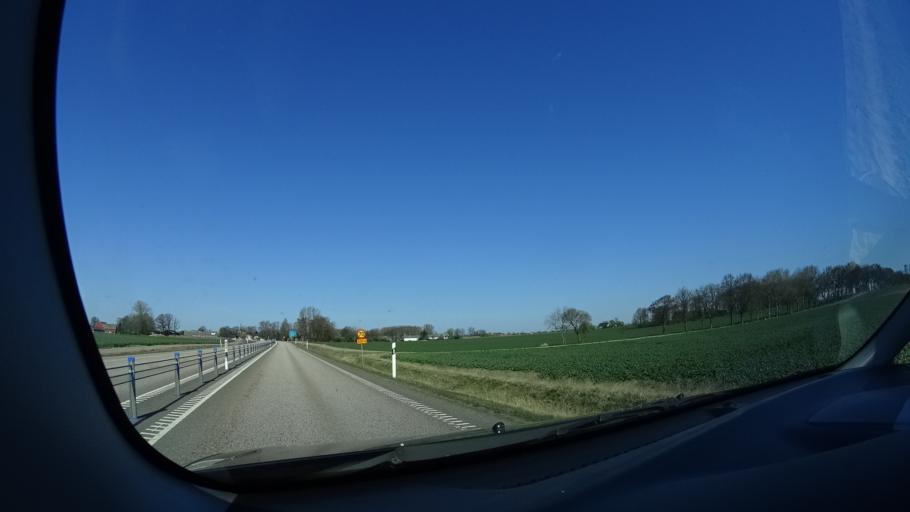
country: SE
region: Skane
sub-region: Angelholms Kommun
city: AEngelholm
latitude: 56.1902
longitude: 12.8681
